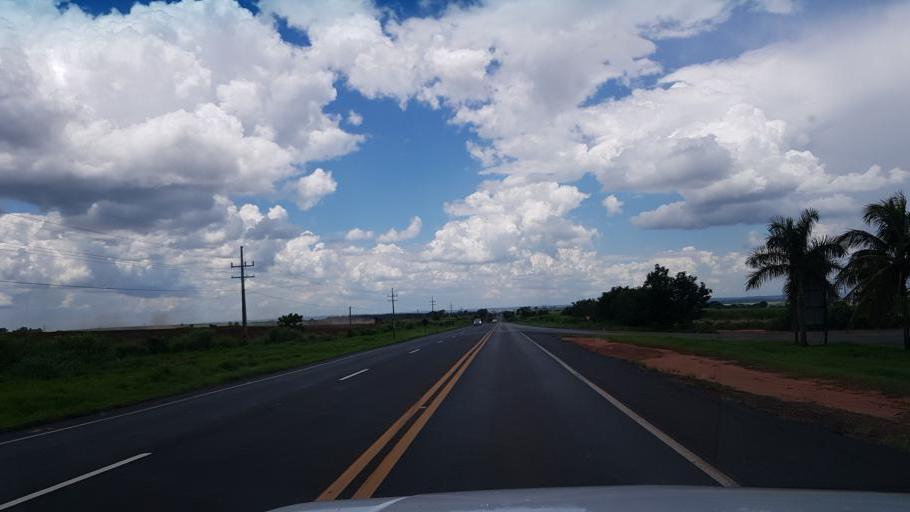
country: BR
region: Sao Paulo
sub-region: Paraguacu Paulista
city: Paraguacu Paulista
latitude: -22.3710
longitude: -50.6255
